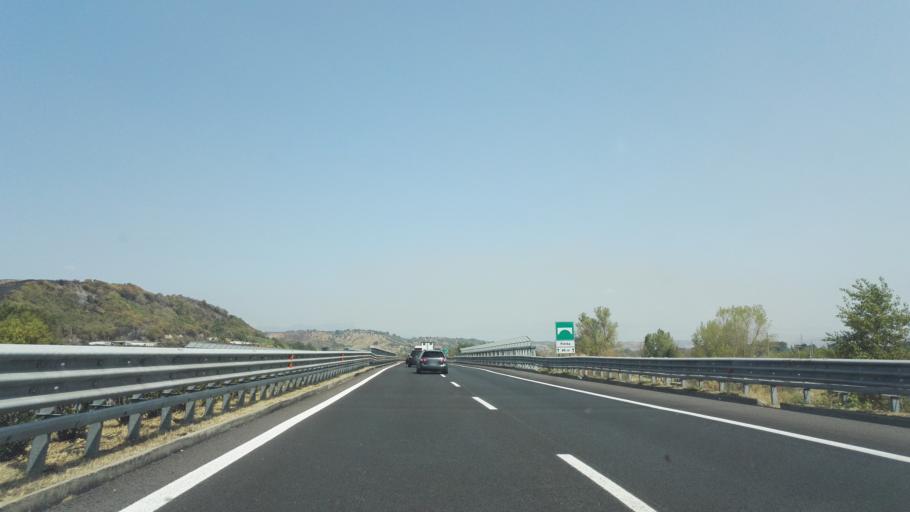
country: IT
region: Calabria
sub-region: Provincia di Cosenza
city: Sartano
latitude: 39.4806
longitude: 16.2151
